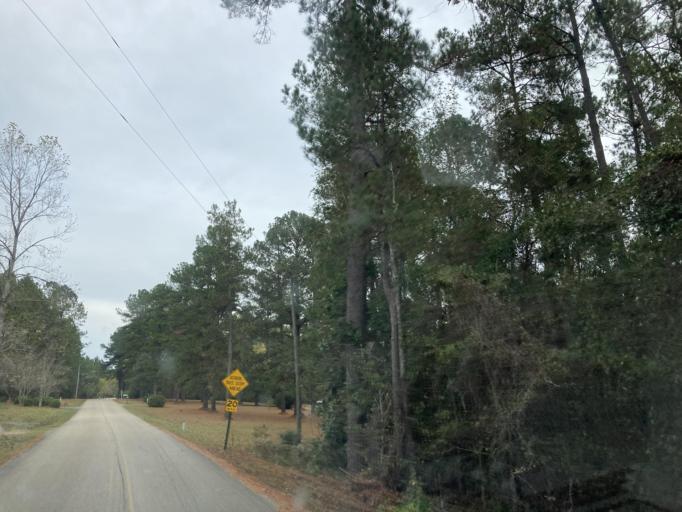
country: US
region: Mississippi
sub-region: Lamar County
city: Purvis
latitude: 31.1405
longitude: -89.4609
